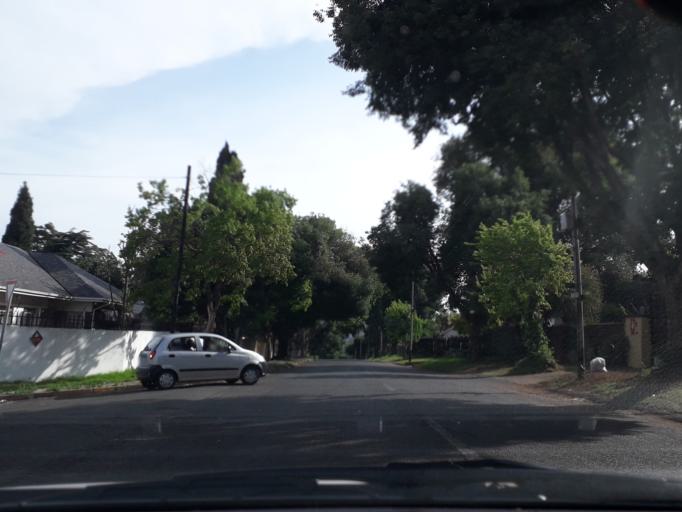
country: ZA
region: Gauteng
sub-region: City of Johannesburg Metropolitan Municipality
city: Johannesburg
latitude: -26.1769
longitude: 28.0974
